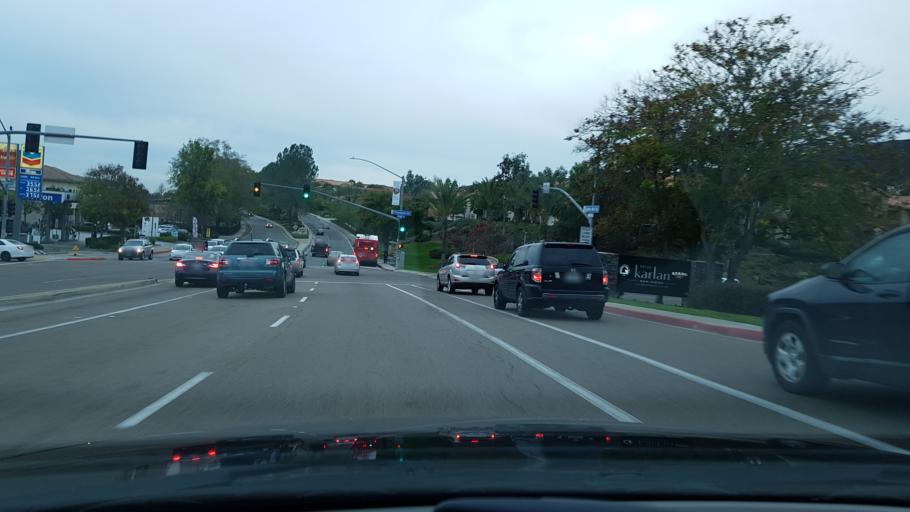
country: US
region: California
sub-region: San Diego County
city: Poway
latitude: 32.9778
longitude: -117.0901
